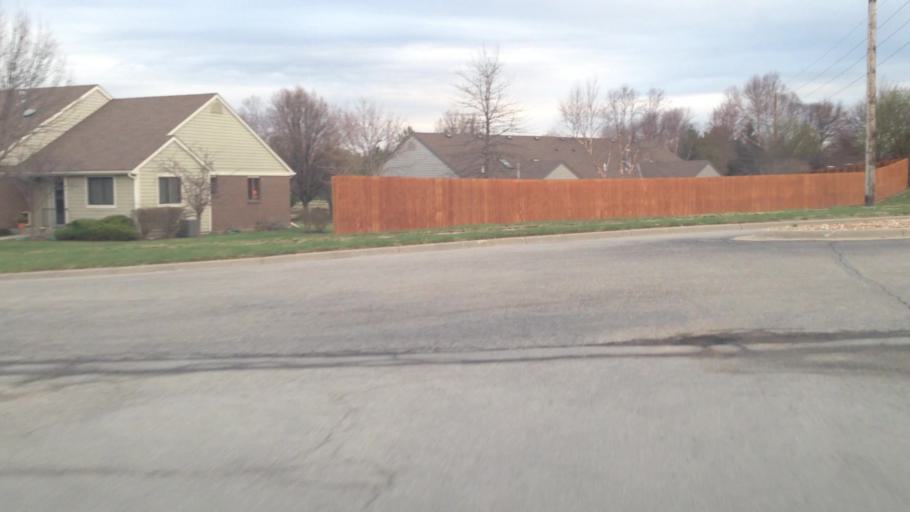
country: US
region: Kansas
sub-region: Douglas County
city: Lawrence
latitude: 38.9548
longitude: -95.3066
